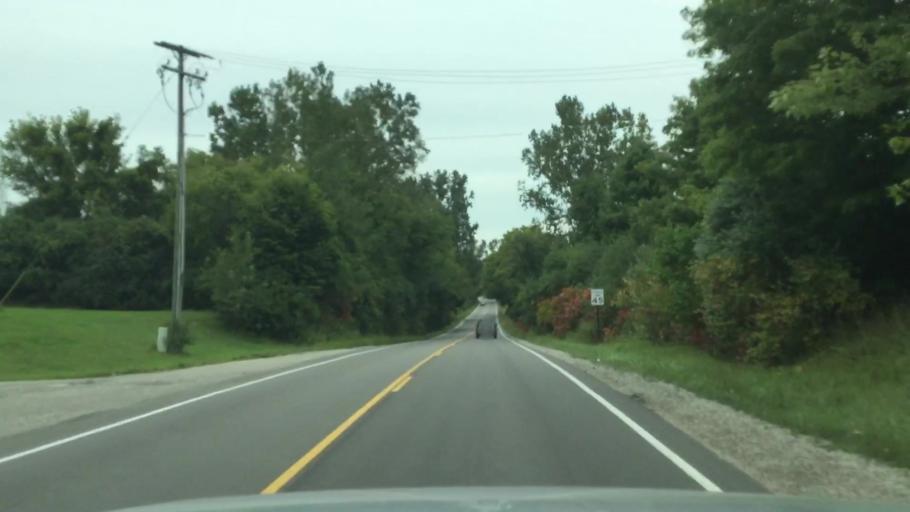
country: US
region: Michigan
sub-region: Washtenaw County
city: Ypsilanti
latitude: 42.2043
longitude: -83.6209
